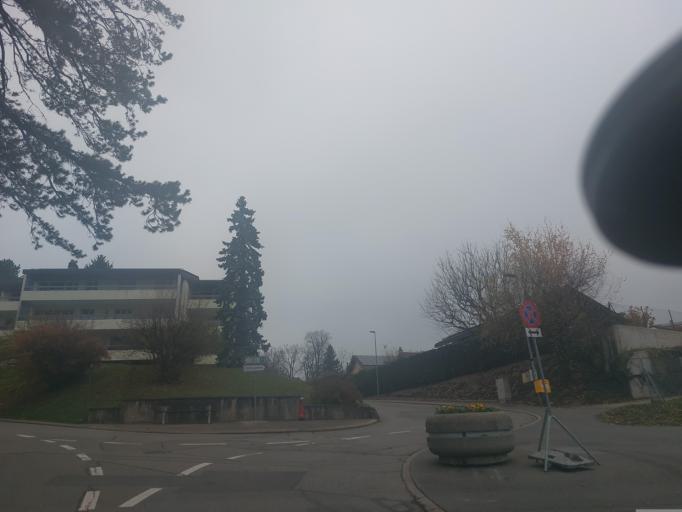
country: CH
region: Vaud
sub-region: Riviera-Pays-d'Enhaut District
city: Blonay
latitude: 46.4741
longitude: 6.8774
